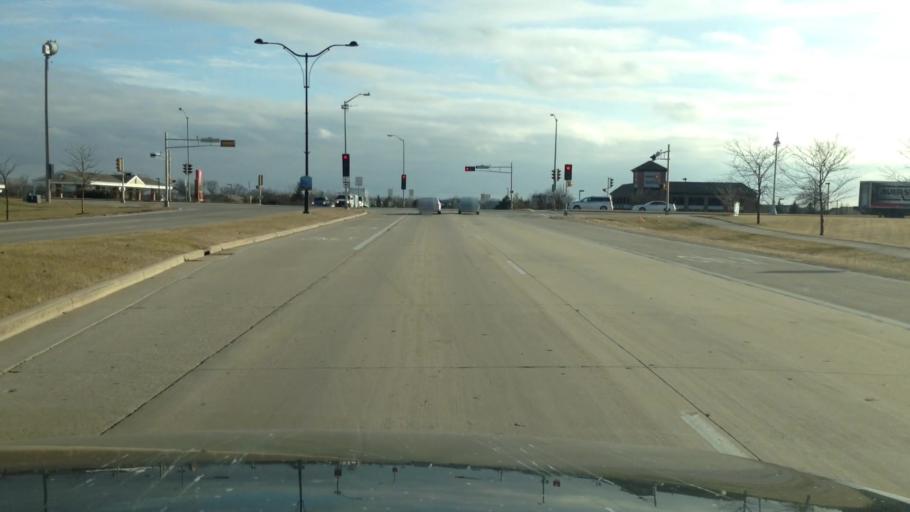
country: US
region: Wisconsin
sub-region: Waukesha County
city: Muskego
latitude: 42.9198
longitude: -88.1093
